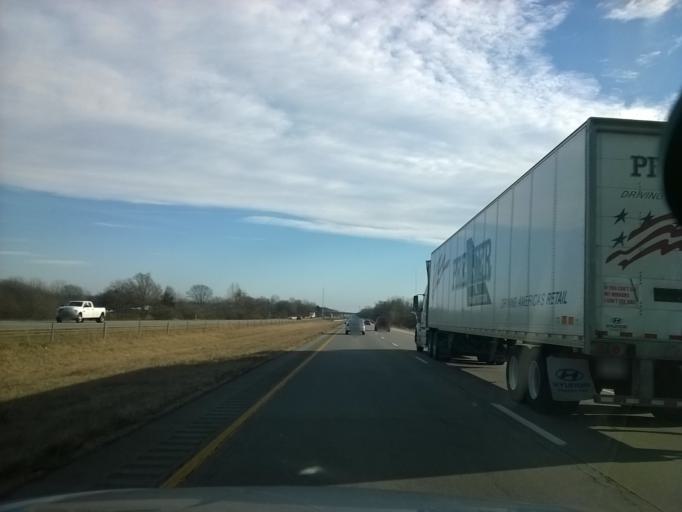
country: US
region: Indiana
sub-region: Johnson County
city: Franklin
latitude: 39.4479
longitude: -85.9932
